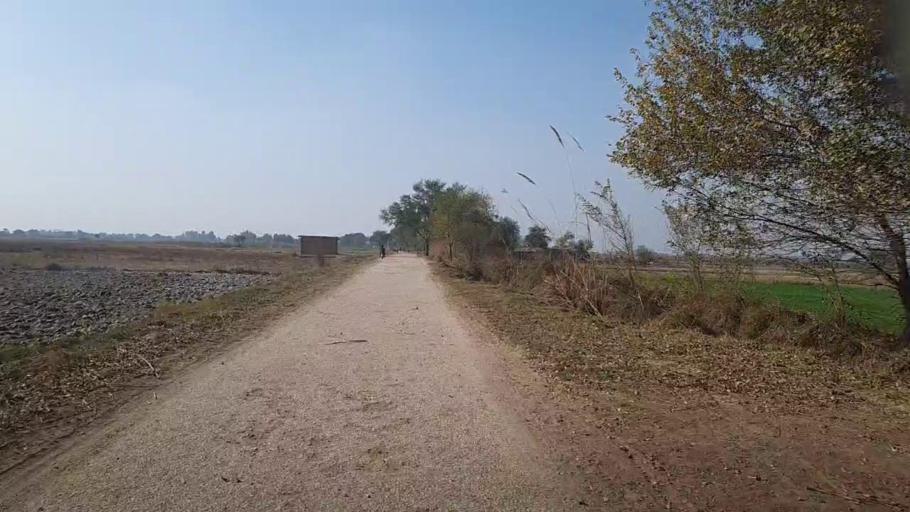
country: PK
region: Sindh
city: Mirpur Mathelo
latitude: 27.9018
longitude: 69.6347
